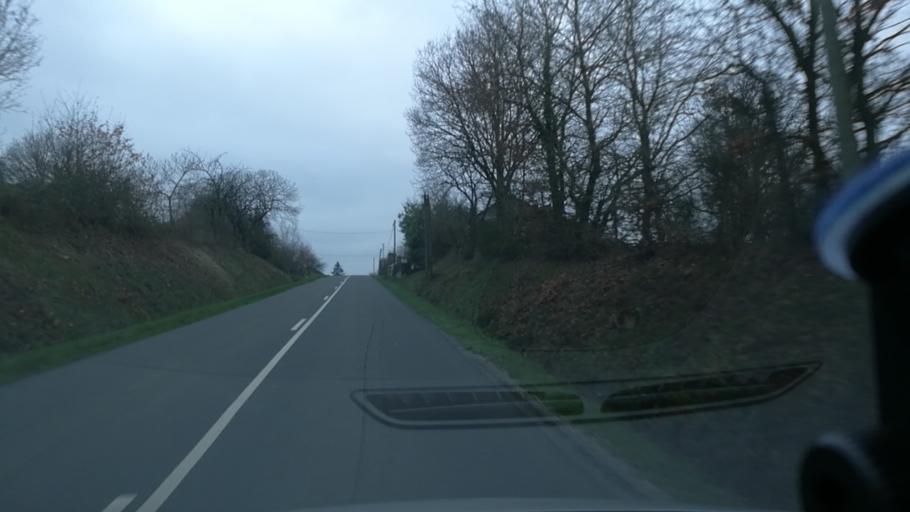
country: FR
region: Brittany
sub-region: Departement d'Ille-et-Vilaine
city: Tresboeuf
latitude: 47.8807
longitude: -1.5139
